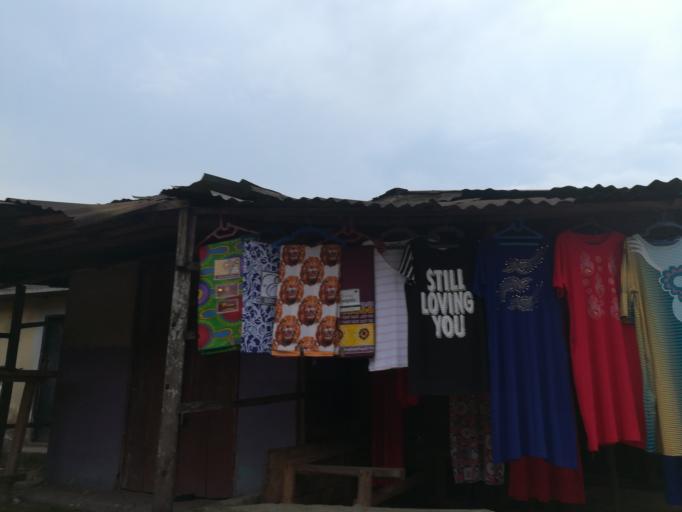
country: NG
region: Rivers
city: Okrika
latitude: 4.7883
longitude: 7.1254
